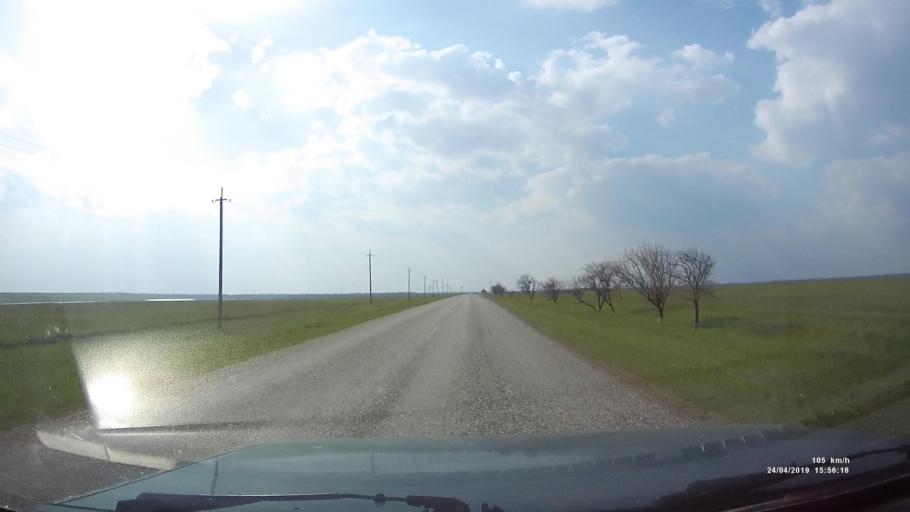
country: RU
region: Kalmykiya
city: Yashalta
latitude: 46.5965
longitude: 42.5322
